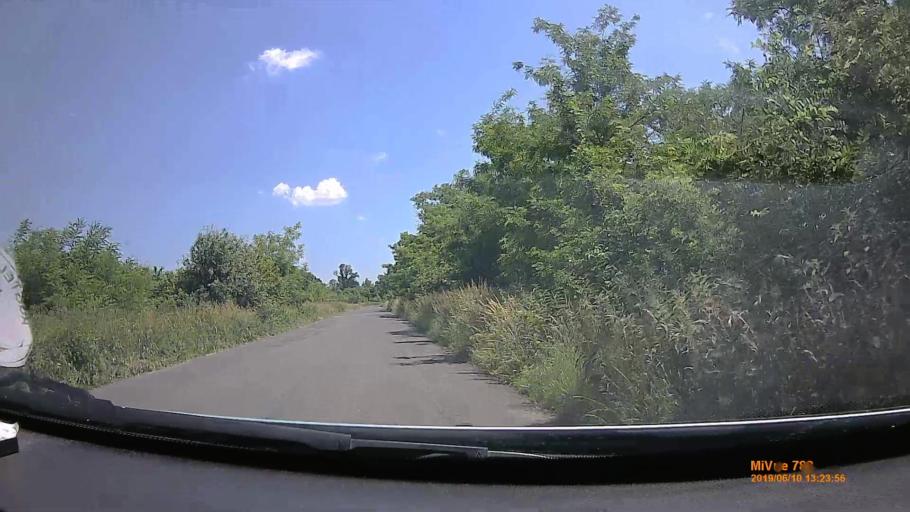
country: HU
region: Borsod-Abauj-Zemplen
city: Tiszaluc
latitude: 48.0236
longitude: 21.0979
